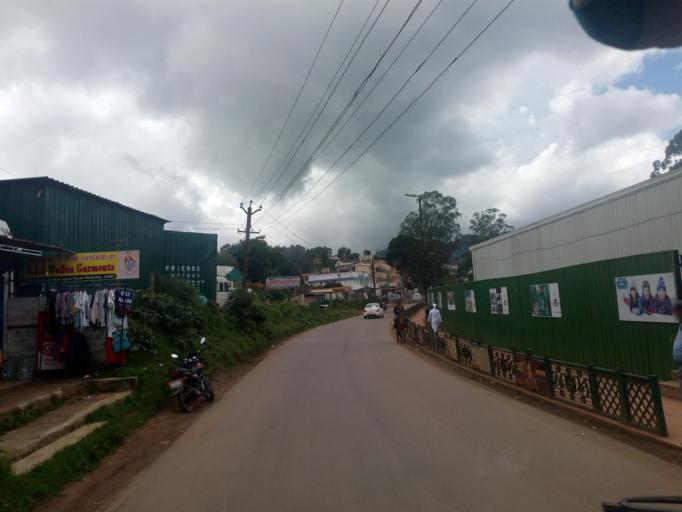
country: IN
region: Tamil Nadu
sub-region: Nilgiri
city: Ooty
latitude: 11.4043
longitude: 76.6939
